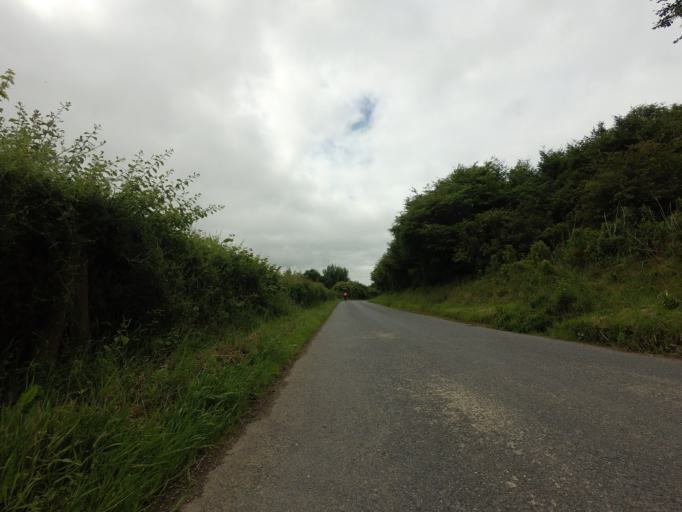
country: GB
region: Scotland
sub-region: Aberdeenshire
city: Rosehearty
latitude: 57.5369
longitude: -2.1857
